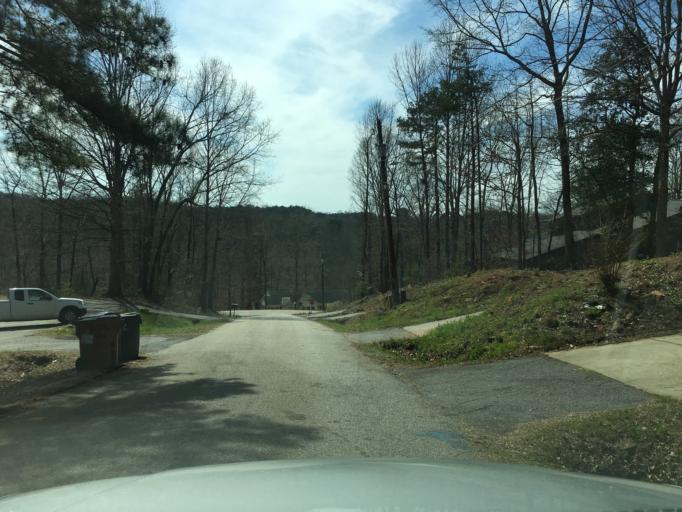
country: US
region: South Carolina
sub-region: Spartanburg County
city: Duncan
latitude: 34.9205
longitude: -82.1238
